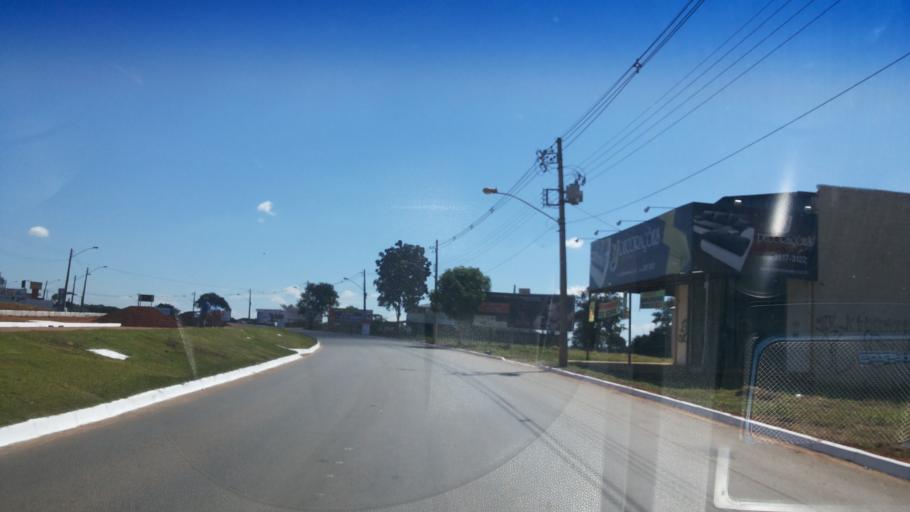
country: BR
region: Goias
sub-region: Goiania
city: Goiania
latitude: -16.6240
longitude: -49.2748
